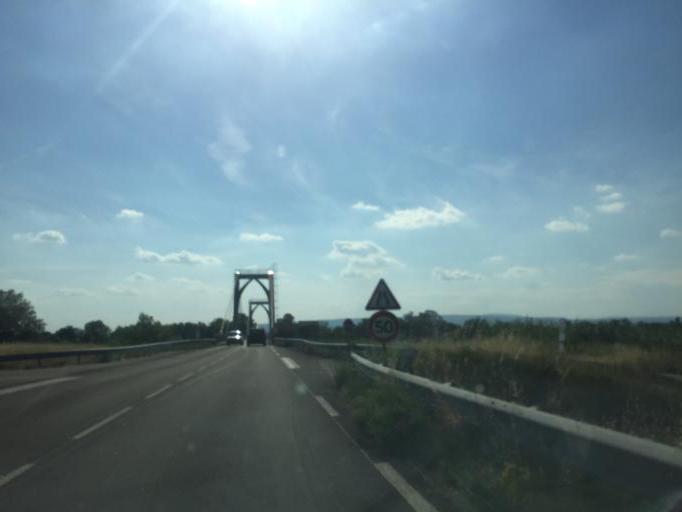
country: FR
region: Rhone-Alpes
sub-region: Departement de la Drome
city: Pierrelatte
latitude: 44.3825
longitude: 4.7302
